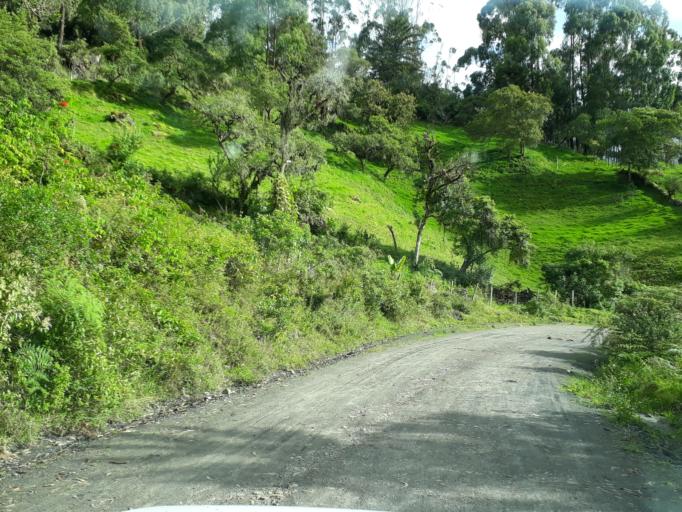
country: CO
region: Cundinamarca
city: Junin
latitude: 4.7845
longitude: -73.6859
